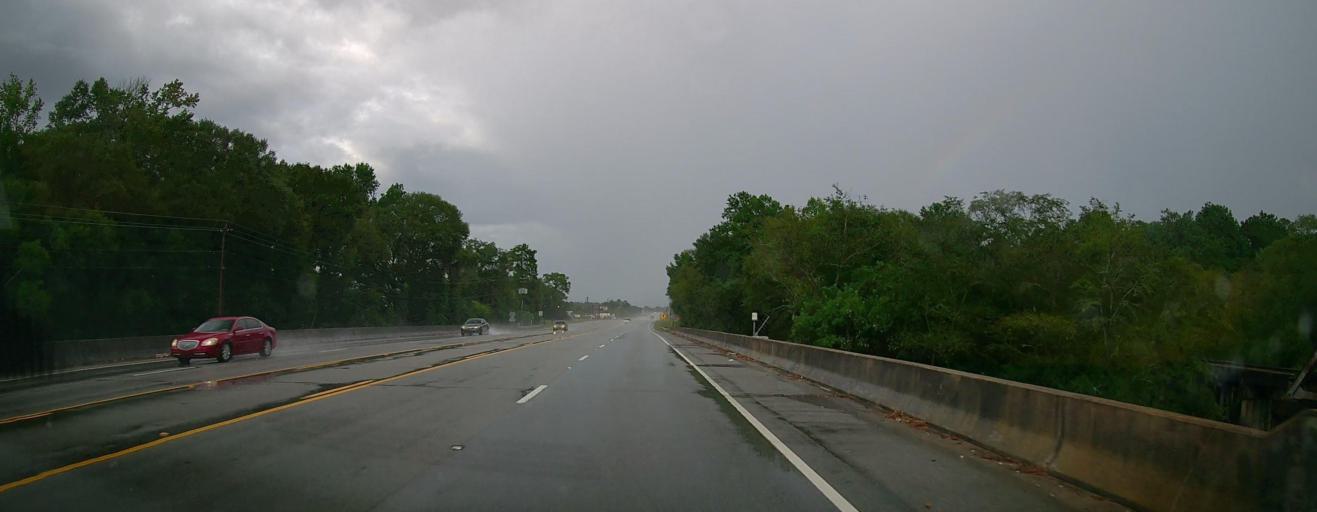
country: US
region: Georgia
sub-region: Ware County
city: Sunnyside
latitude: 31.2382
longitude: -82.3231
